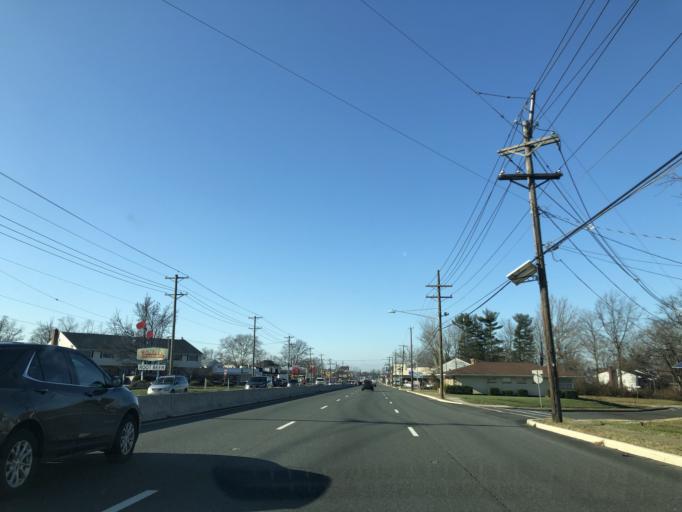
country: US
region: New Jersey
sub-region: Camden County
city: Merchantville
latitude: 39.9357
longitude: -75.0579
